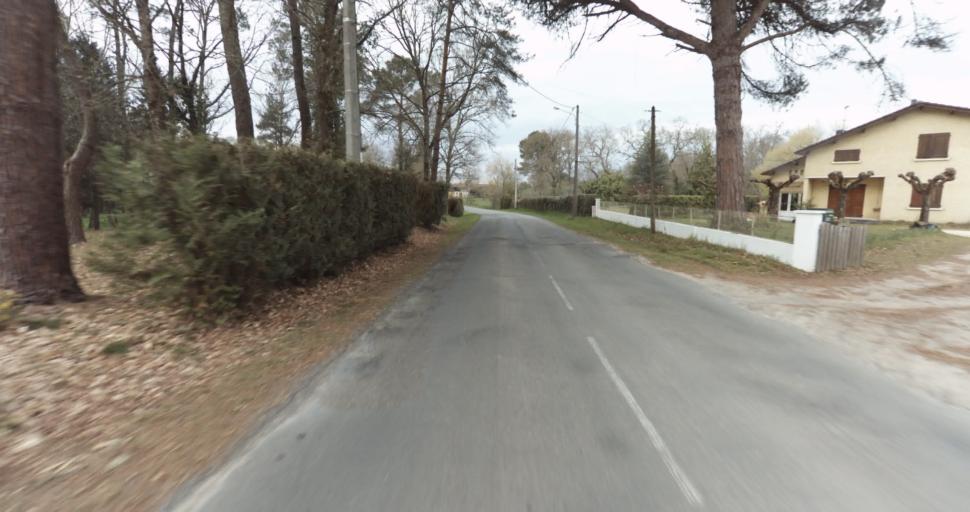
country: FR
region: Aquitaine
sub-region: Departement des Landes
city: Sarbazan
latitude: 44.0197
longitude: -0.3187
